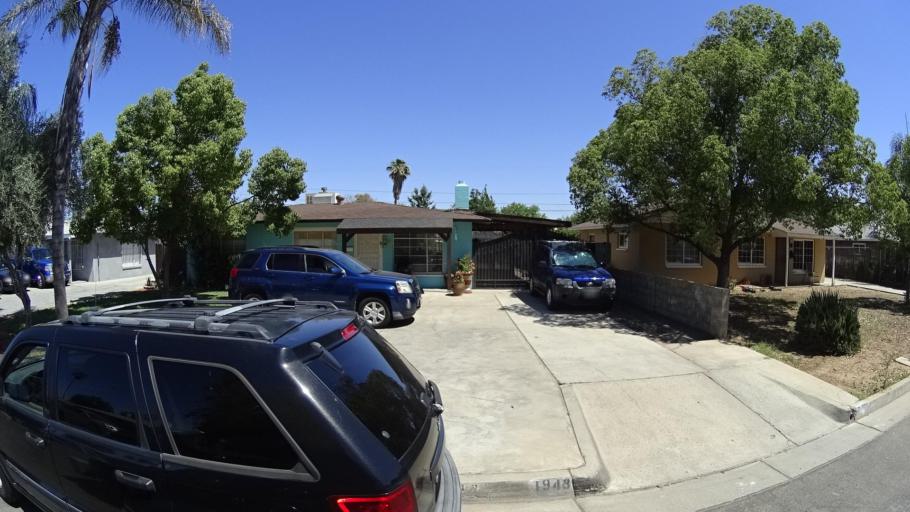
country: US
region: California
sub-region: Fresno County
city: Fresno
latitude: 36.7968
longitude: -119.7871
